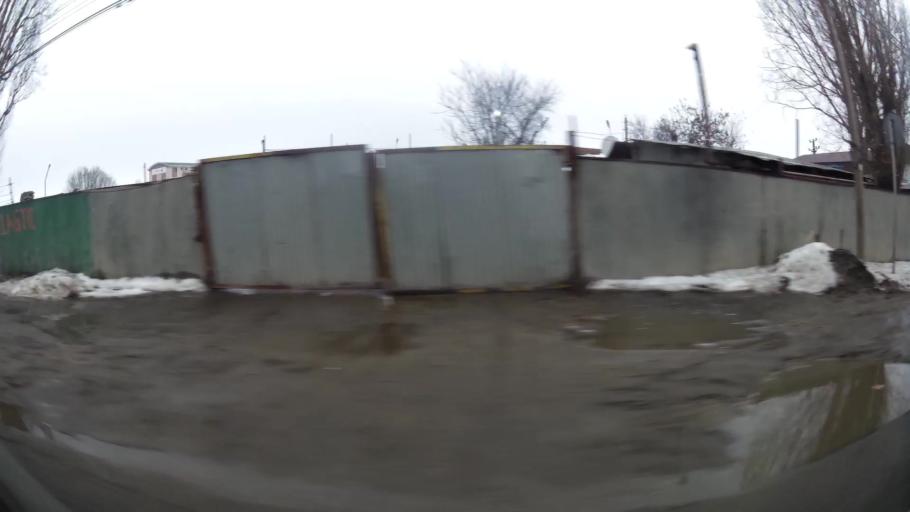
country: RO
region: Ilfov
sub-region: Comuna Bragadiru
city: Bragadiru
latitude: 44.3846
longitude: 25.9911
